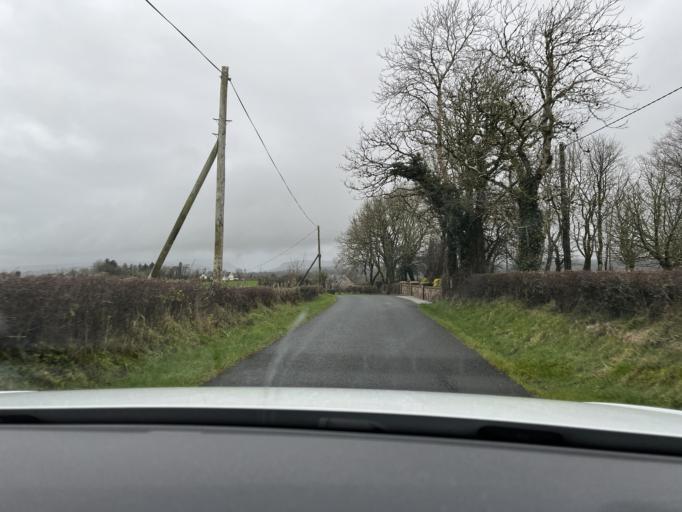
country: IE
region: Connaught
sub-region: County Leitrim
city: Manorhamilton
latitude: 54.2971
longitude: -8.1410
